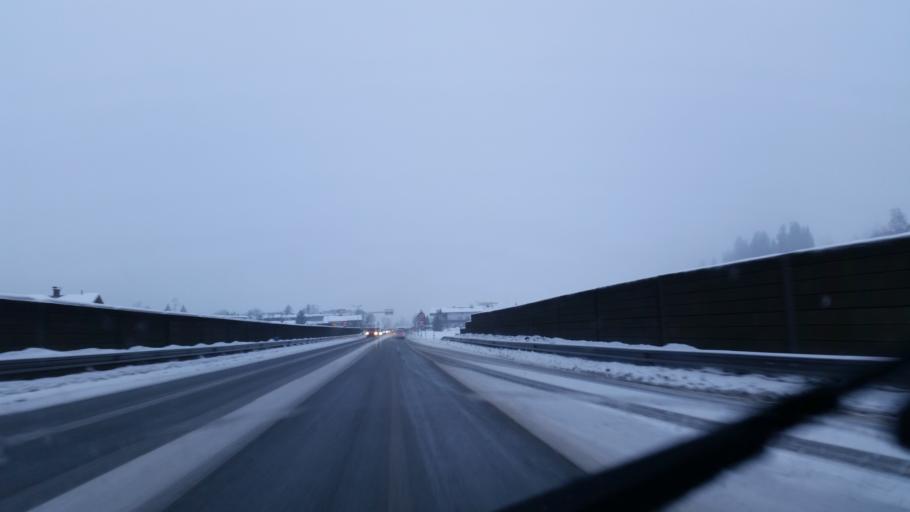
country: AT
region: Tyrol
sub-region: Politischer Bezirk Kufstein
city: Ellmau
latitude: 47.5152
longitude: 12.3280
